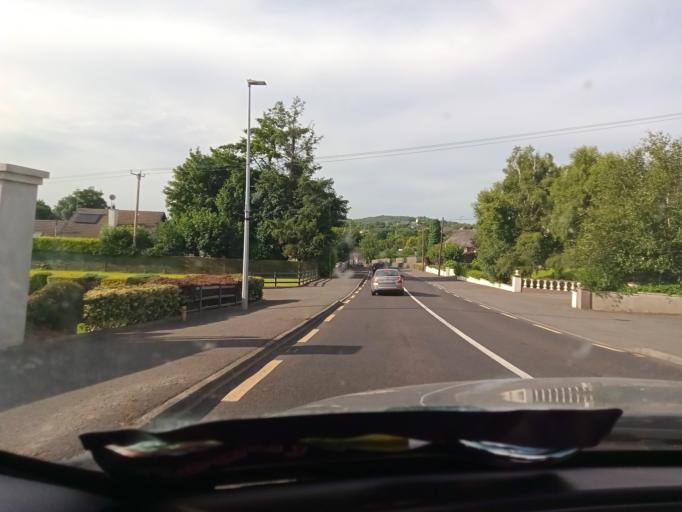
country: IE
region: Ulster
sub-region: An Cabhan
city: Cavan
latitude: 53.9274
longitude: -7.4123
